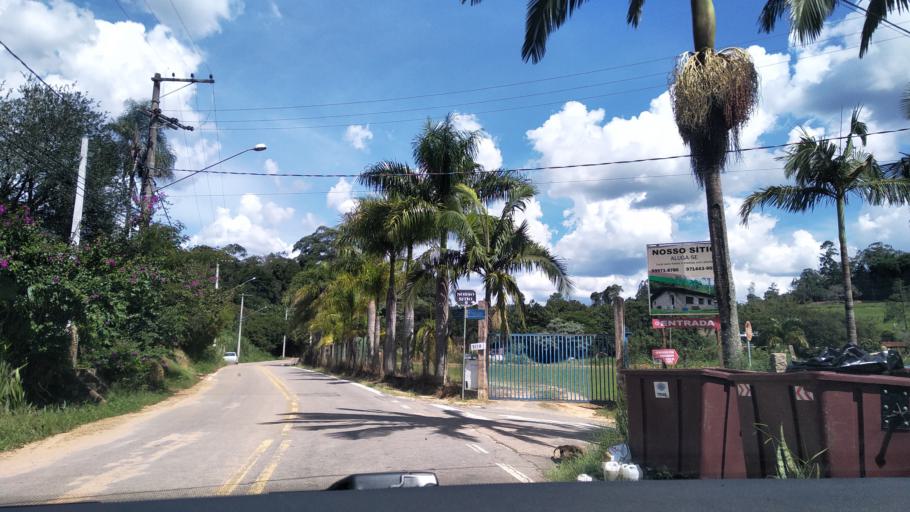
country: BR
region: Sao Paulo
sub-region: Varzea Paulista
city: Varzea Paulista
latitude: -23.2638
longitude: -46.8826
